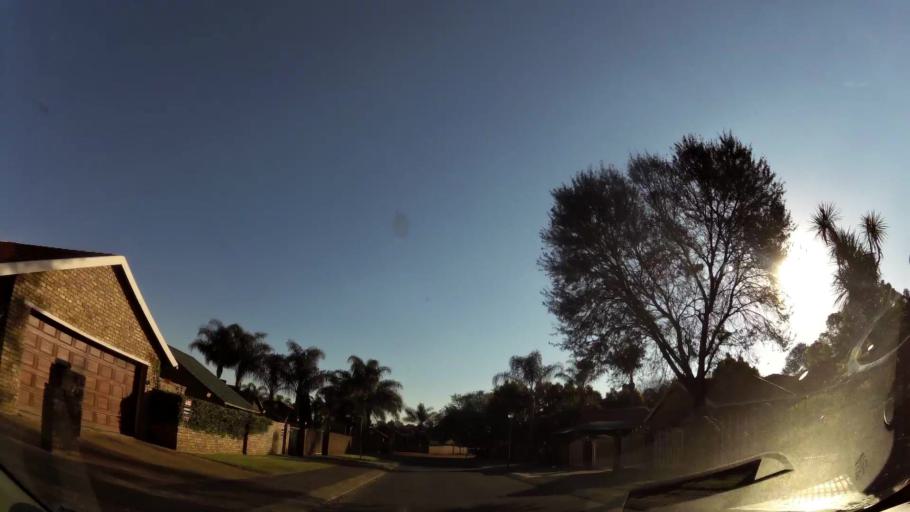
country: ZA
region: Gauteng
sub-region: City of Tshwane Metropolitan Municipality
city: Centurion
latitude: -25.8561
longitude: 28.1527
